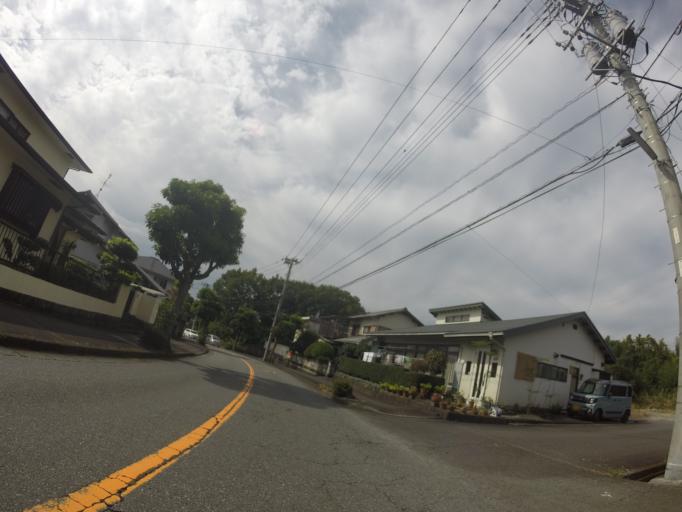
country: JP
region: Shizuoka
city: Fuji
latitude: 35.1865
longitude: 138.7087
